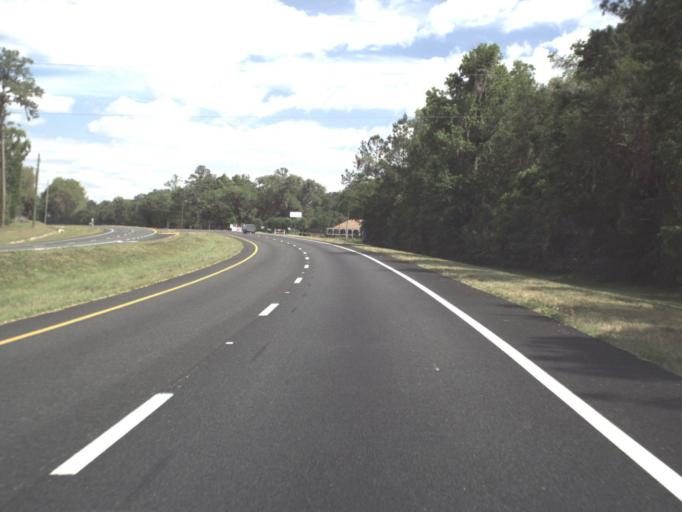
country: US
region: Florida
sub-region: Levy County
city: Williston
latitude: 29.2615
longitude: -82.3235
